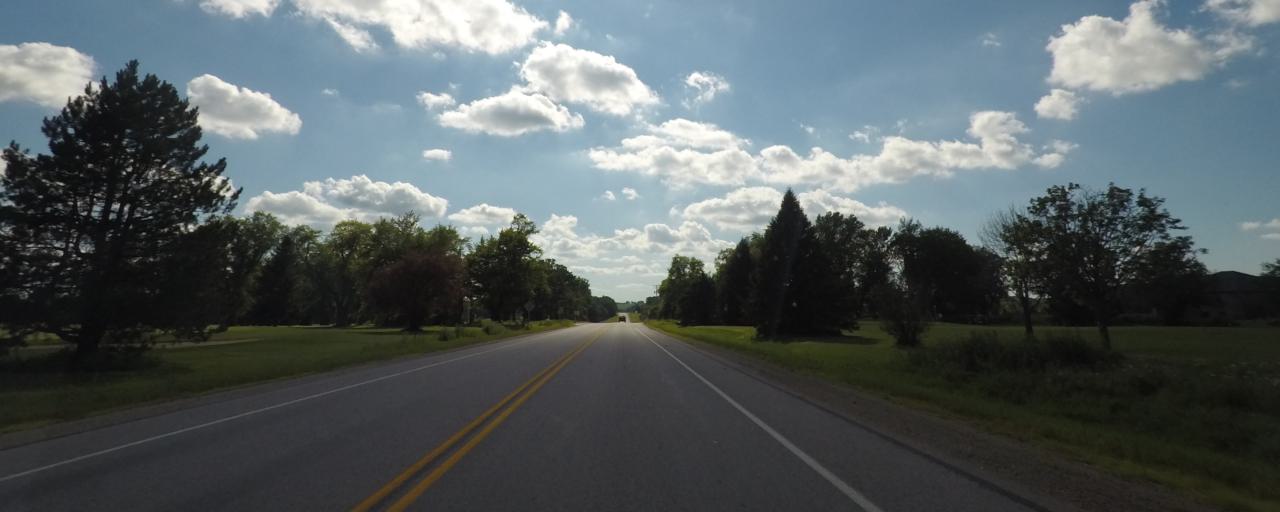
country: US
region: Wisconsin
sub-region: Rock County
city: Edgerton
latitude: 42.9206
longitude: -89.0967
